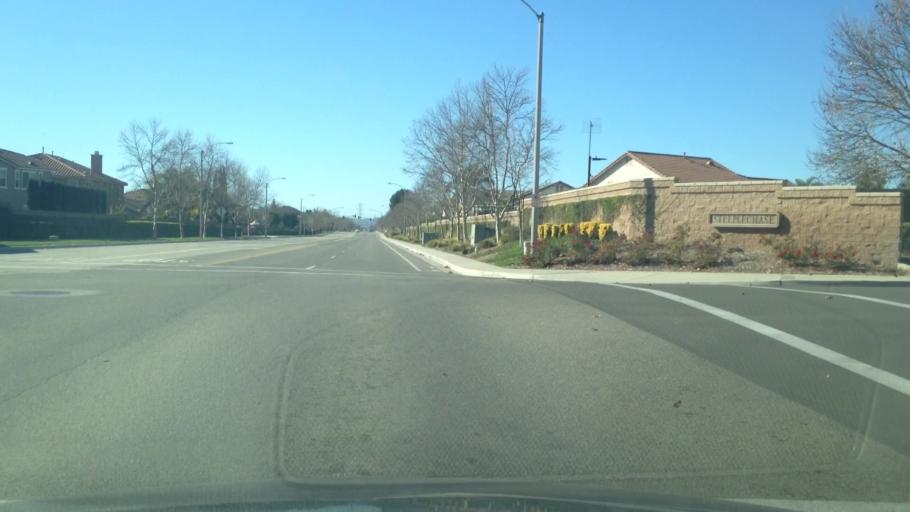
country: US
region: California
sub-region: Riverside County
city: Norco
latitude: 33.9682
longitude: -117.5799
